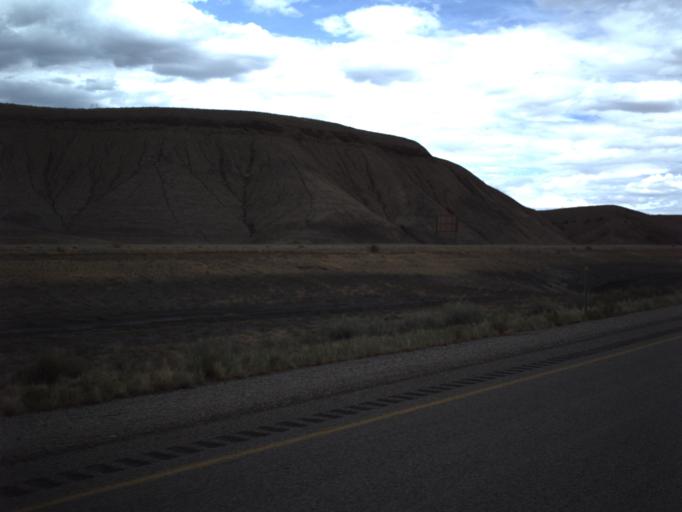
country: US
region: Utah
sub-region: Carbon County
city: East Carbon City
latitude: 38.9706
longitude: -110.0990
